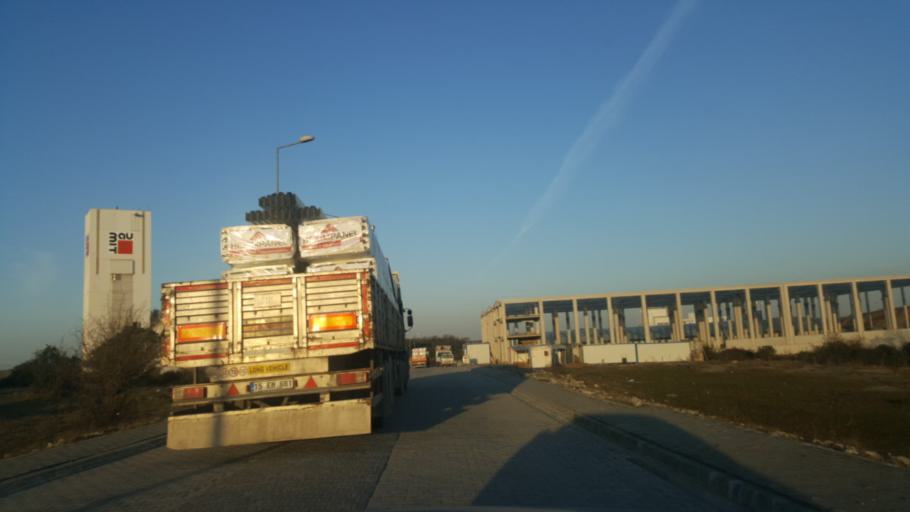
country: TR
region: Kocaeli
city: Mollafeneri
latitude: 40.8690
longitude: 29.5552
